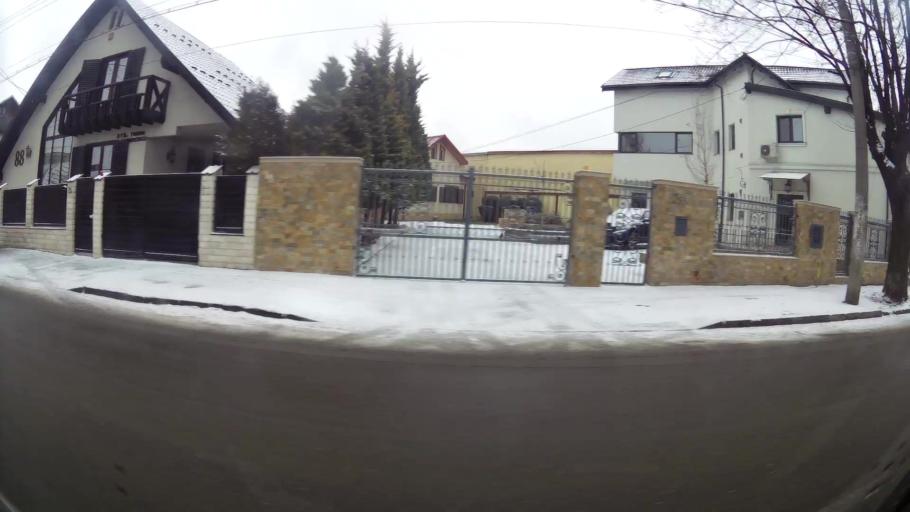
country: RO
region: Prahova
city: Ploiesti
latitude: 44.9347
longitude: 26.0078
